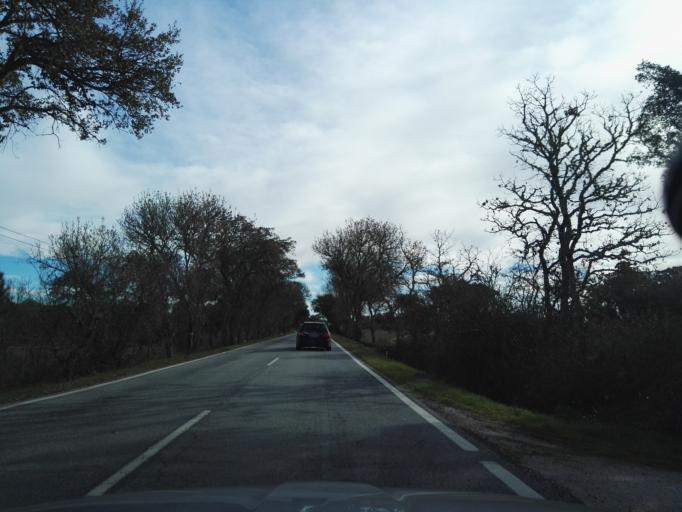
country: PT
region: Portalegre
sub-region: Nisa
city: Nisa
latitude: 39.5000
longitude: -7.6801
